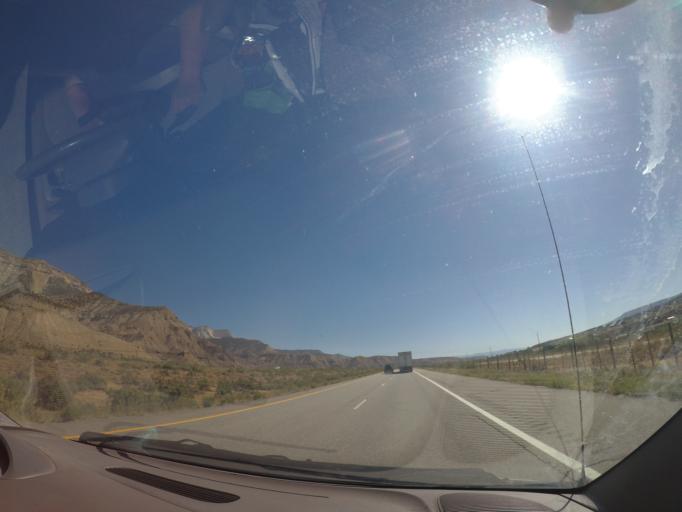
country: US
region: Colorado
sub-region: Garfield County
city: Battlement Mesa
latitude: 39.4883
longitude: -107.9560
